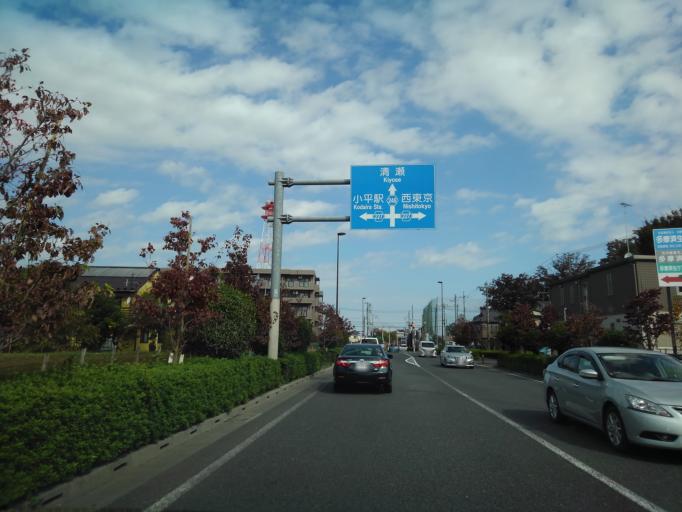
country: JP
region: Tokyo
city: Tanashicho
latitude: 35.7362
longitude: 139.4997
